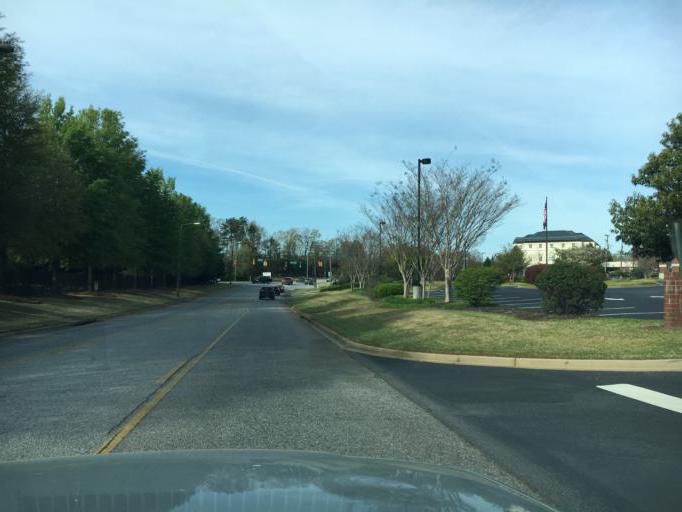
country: US
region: South Carolina
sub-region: Greenville County
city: Greenville
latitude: 34.8380
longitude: -82.3366
